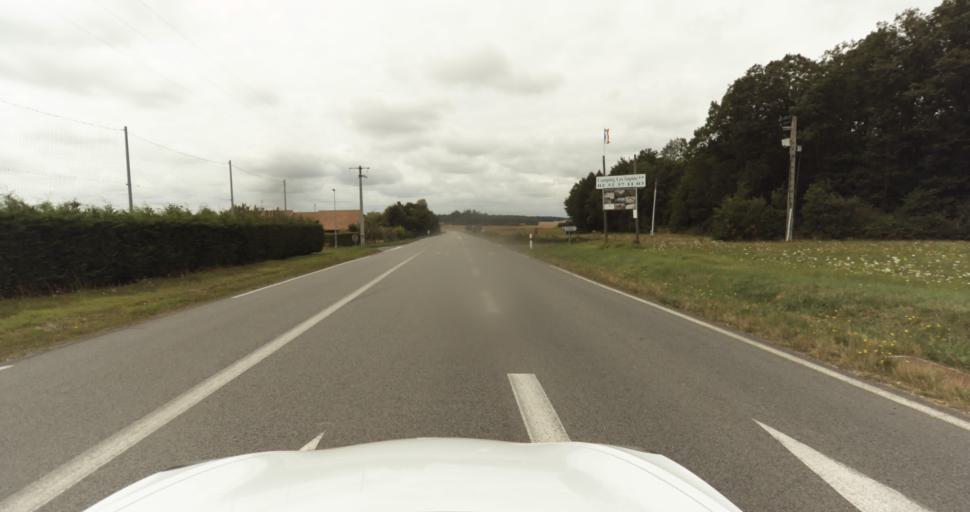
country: FR
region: Haute-Normandie
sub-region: Departement de l'Eure
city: Claville
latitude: 48.9999
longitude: 1.0355
